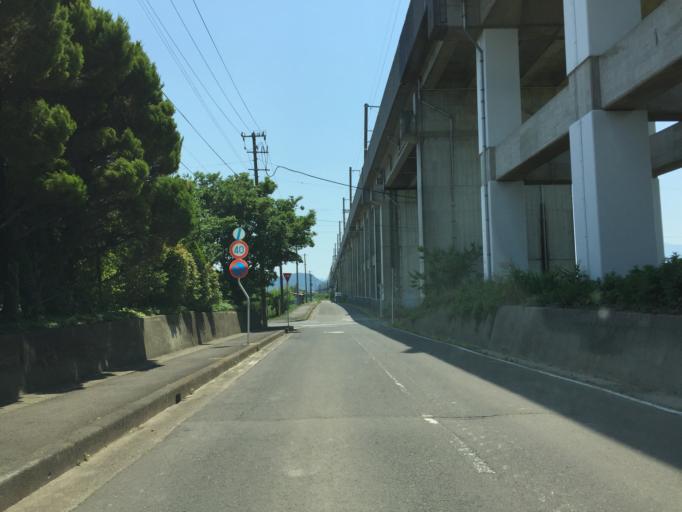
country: JP
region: Fukushima
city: Hobaramachi
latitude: 37.8171
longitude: 140.4892
